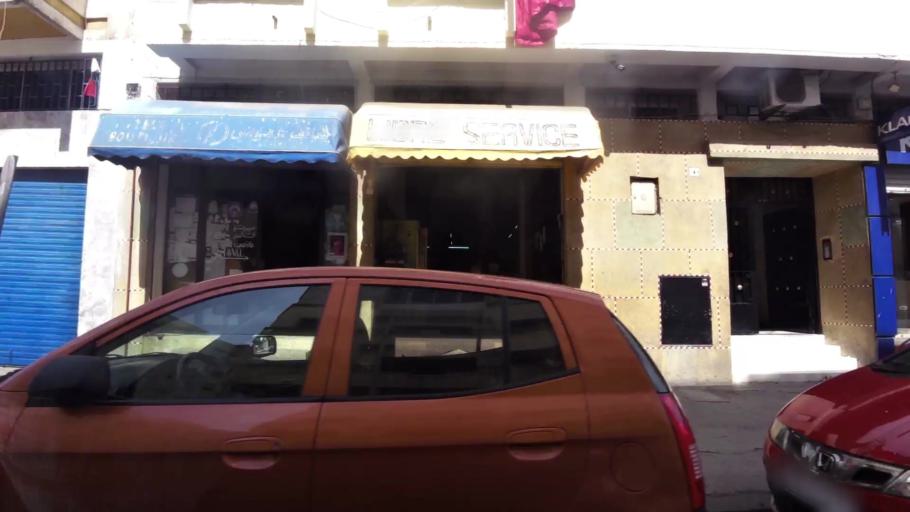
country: MA
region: Grand Casablanca
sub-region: Casablanca
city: Casablanca
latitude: 33.5802
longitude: -7.6381
